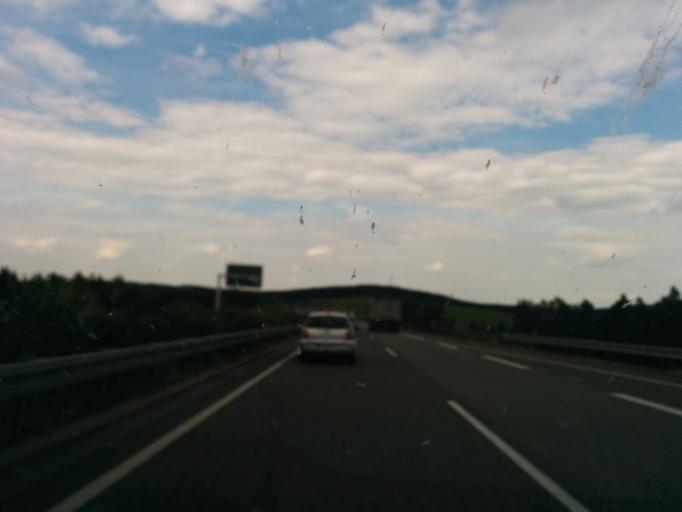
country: DE
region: Thuringia
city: Langewiesen
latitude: 50.7162
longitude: 10.9669
